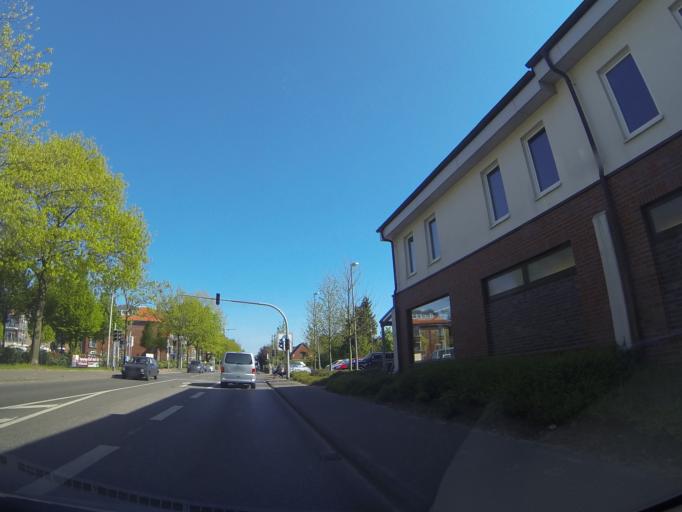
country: DE
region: Schleswig-Holstein
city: Halstenbek
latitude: 53.6346
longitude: 9.8376
